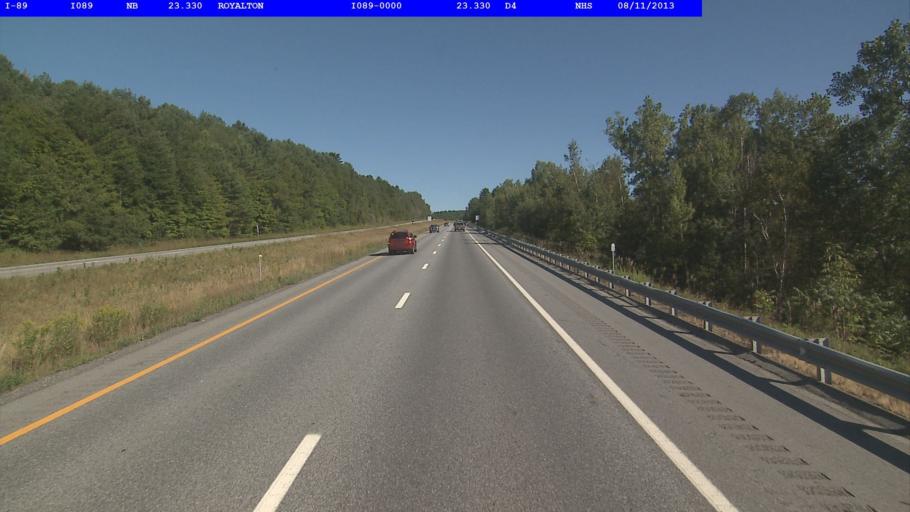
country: US
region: Vermont
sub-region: Orange County
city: Randolph
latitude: 43.8399
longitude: -72.5939
